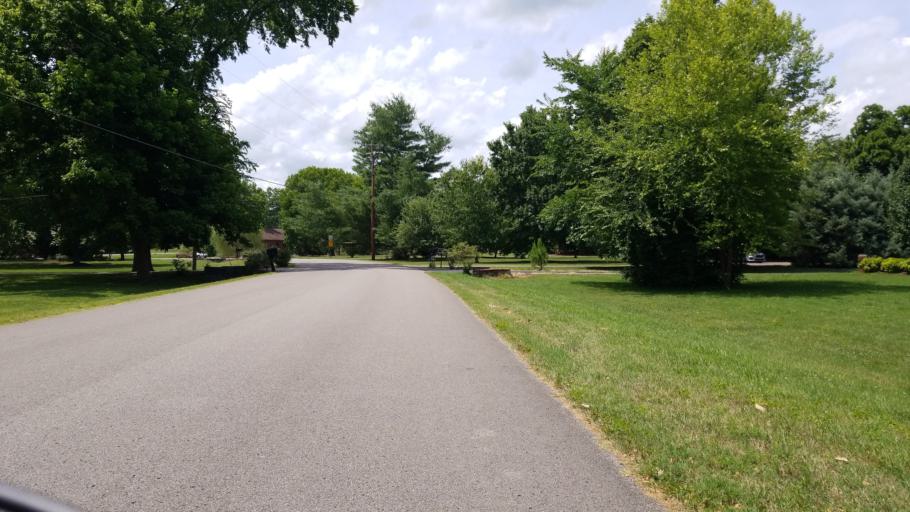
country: US
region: Tennessee
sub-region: Davidson County
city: Forest Hills
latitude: 36.0388
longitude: -86.8430
